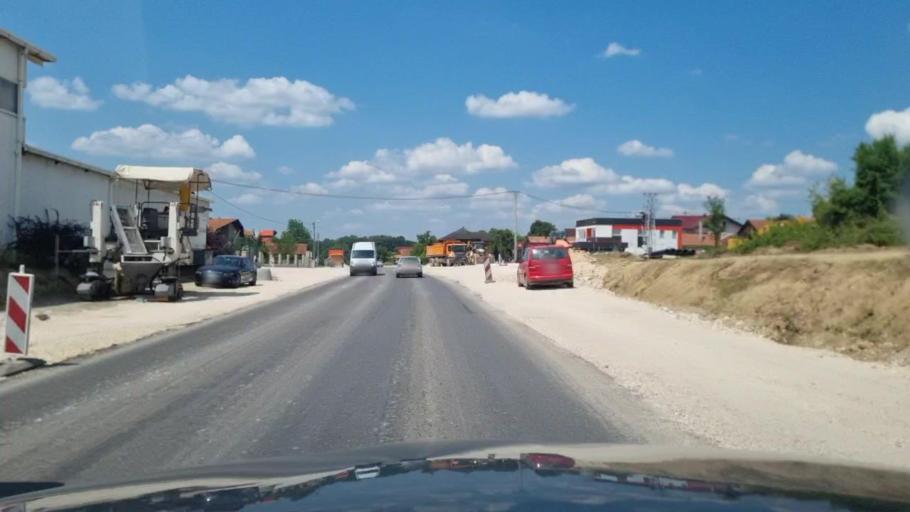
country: BA
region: Federation of Bosnia and Herzegovina
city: Srebrenik
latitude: 44.7145
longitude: 18.4908
